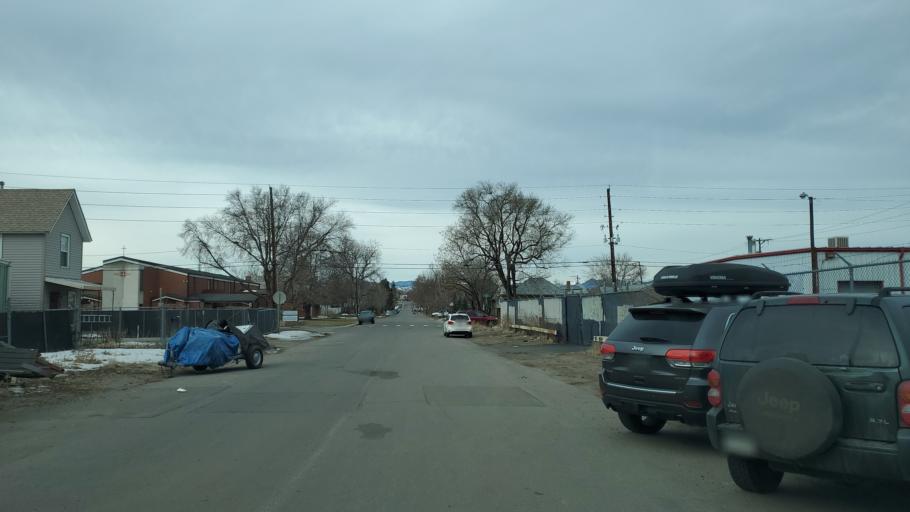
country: US
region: Colorado
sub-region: Denver County
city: Denver
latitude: 39.7103
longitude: -105.0030
